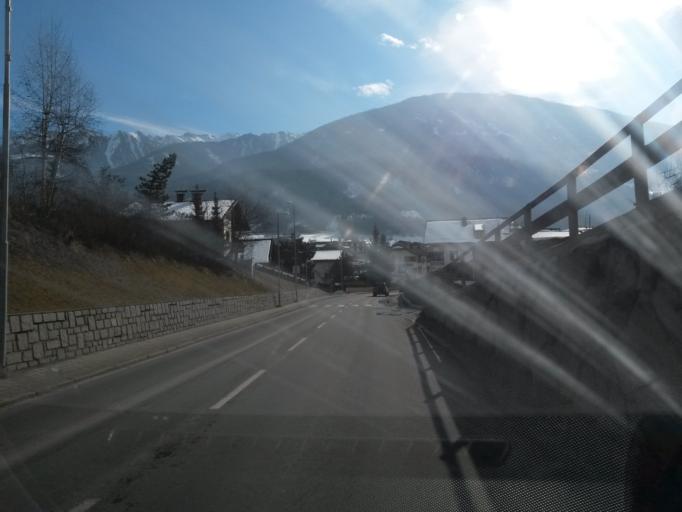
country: AT
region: Tyrol
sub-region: Politischer Bezirk Imst
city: Karrosten
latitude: 47.2096
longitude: 10.7604
